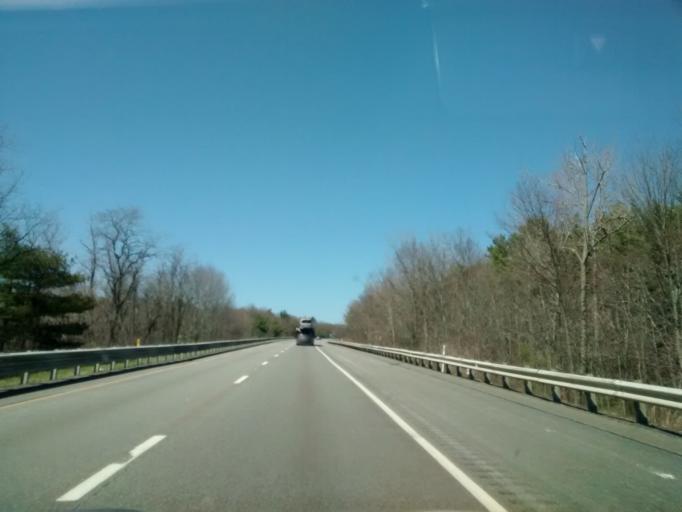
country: US
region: Massachusetts
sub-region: Worcester County
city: Oxford
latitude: 42.1233
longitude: -71.8564
